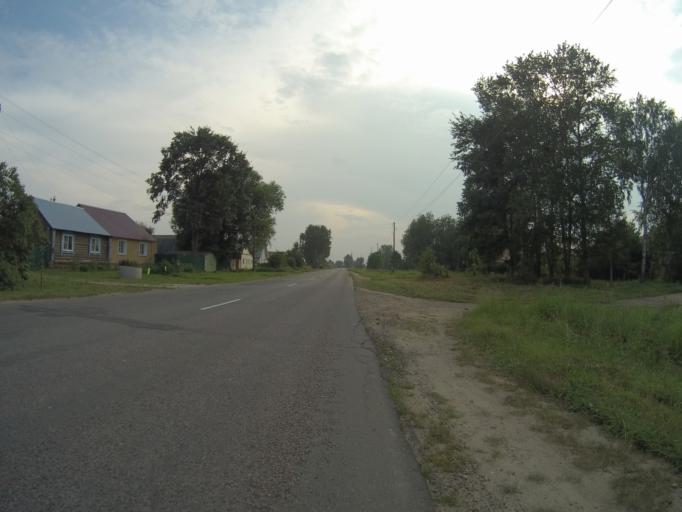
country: RU
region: Vladimir
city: Suzdal'
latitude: 56.4074
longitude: 40.3485
